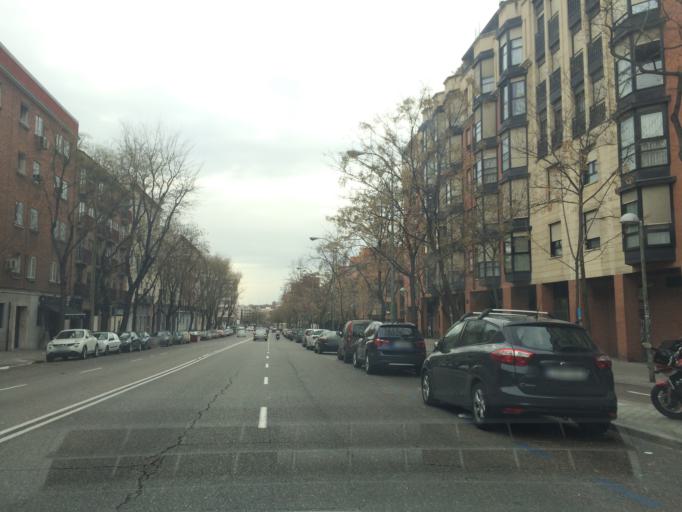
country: ES
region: Madrid
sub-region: Provincia de Madrid
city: Madrid
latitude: 40.4129
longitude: -3.7174
